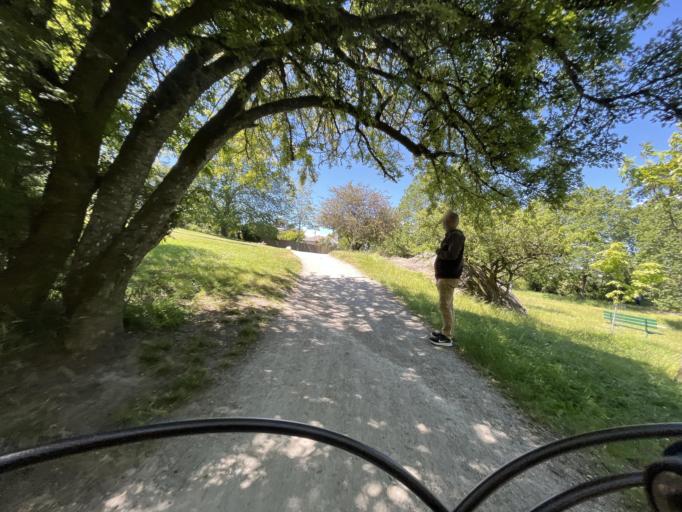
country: CA
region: British Columbia
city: Victoria
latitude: 48.4383
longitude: -123.3876
